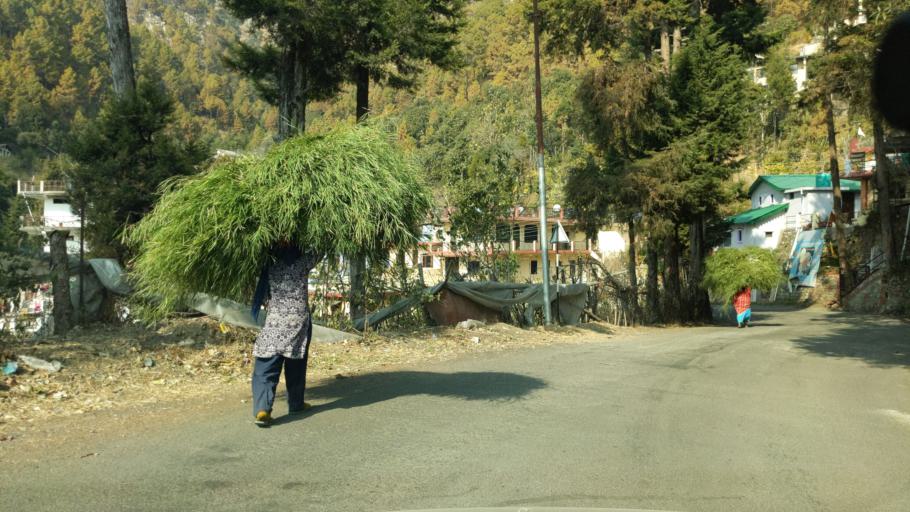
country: IN
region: Uttarakhand
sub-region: Naini Tal
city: Bhowali
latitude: 29.3914
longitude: 79.5336
